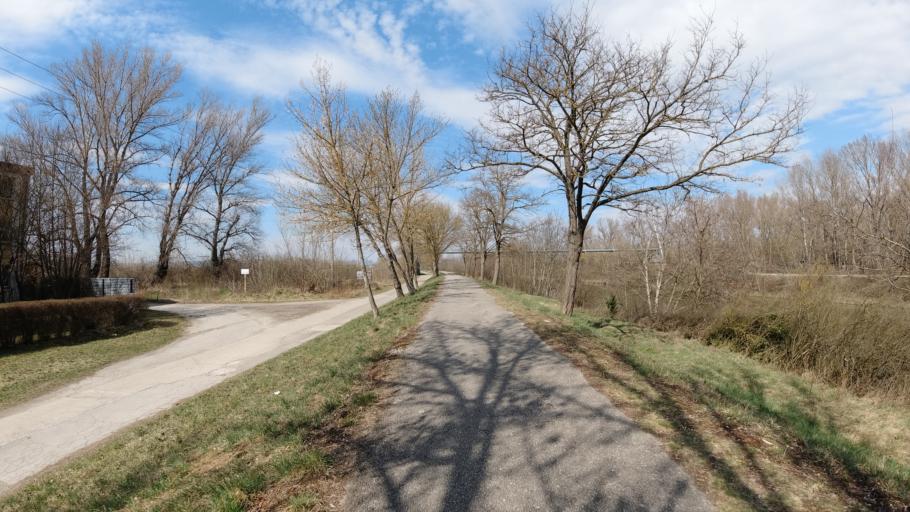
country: SK
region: Trnavsky
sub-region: Okres Trnava
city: Piestany
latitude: 48.6071
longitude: 17.8405
